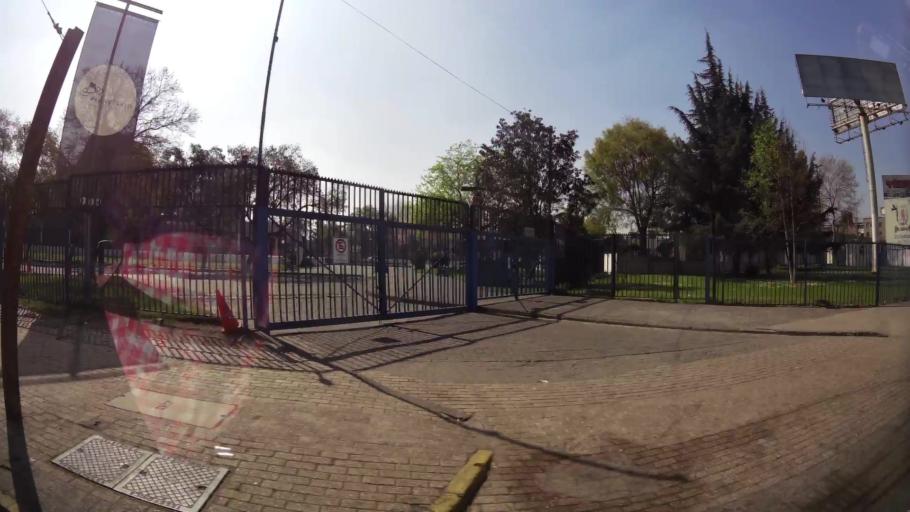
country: CL
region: Santiago Metropolitan
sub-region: Provincia de Santiago
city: Santiago
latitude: -33.4510
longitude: -70.6808
